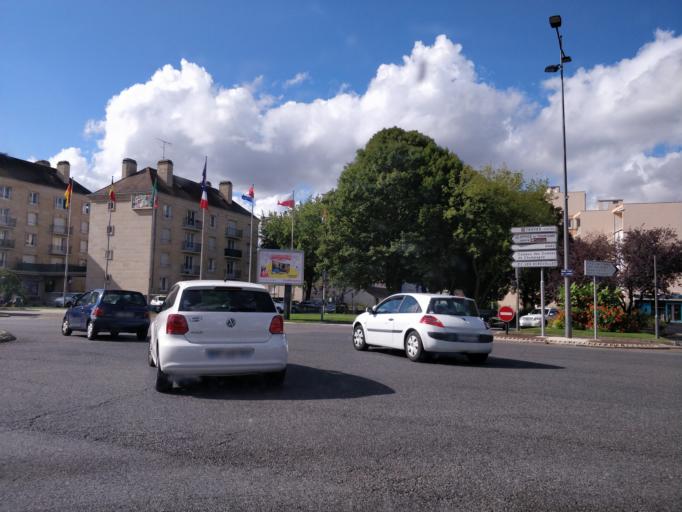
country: FR
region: Champagne-Ardenne
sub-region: Departement de l'Aube
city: Troyes
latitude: 48.3054
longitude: 4.0925
